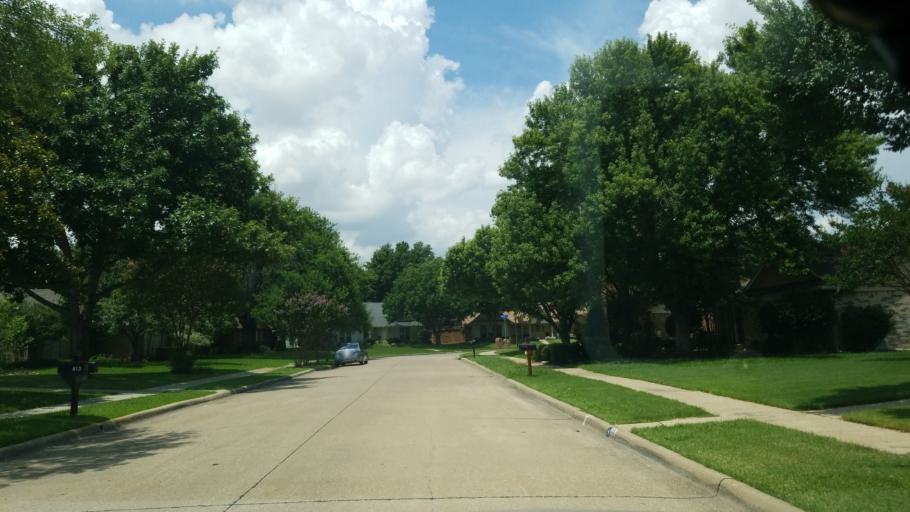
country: US
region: Texas
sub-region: Dallas County
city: Coppell
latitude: 32.9641
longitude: -96.9683
